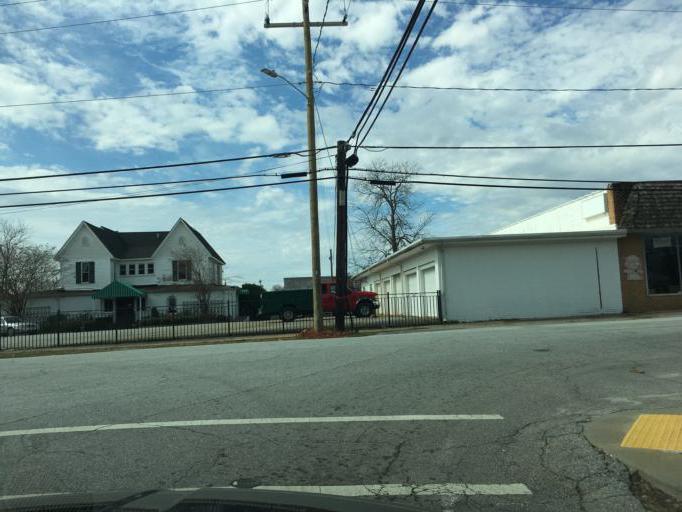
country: US
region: South Carolina
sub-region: Greenville County
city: Fountain Inn
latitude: 34.6927
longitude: -82.1975
